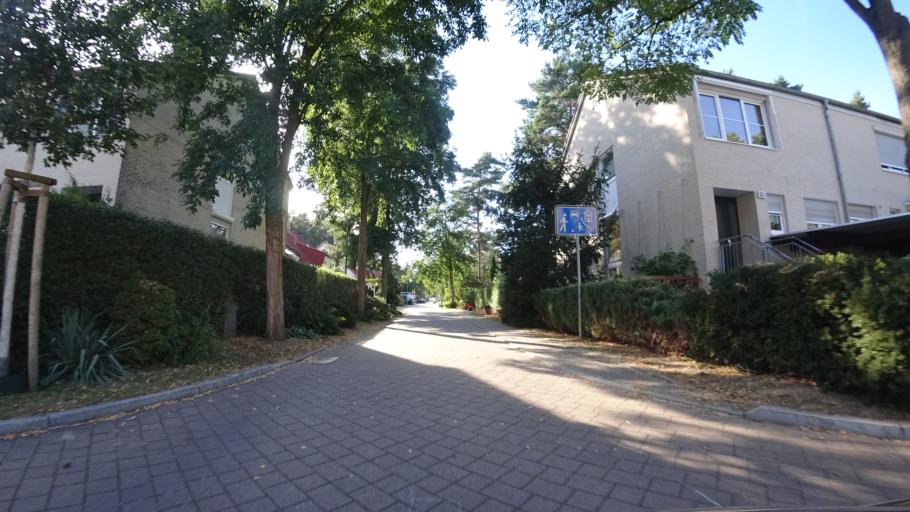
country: DE
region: Brandenburg
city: Stahnsdorf
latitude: 52.3984
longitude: 13.2039
